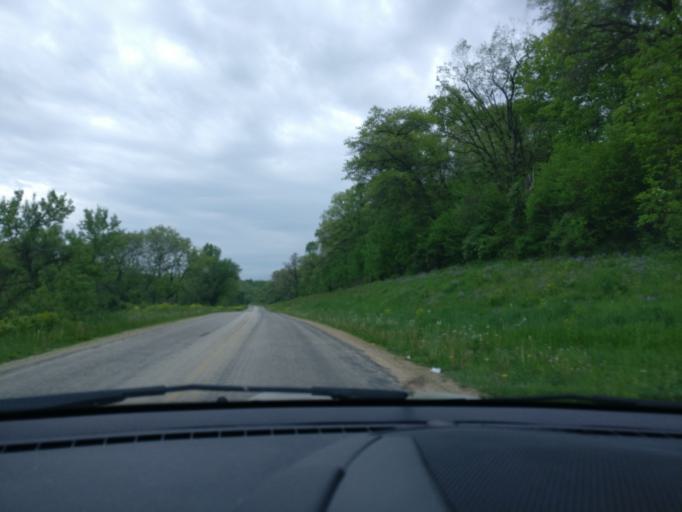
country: US
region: Wisconsin
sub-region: Lafayette County
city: Darlington
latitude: 42.7722
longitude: -90.0028
